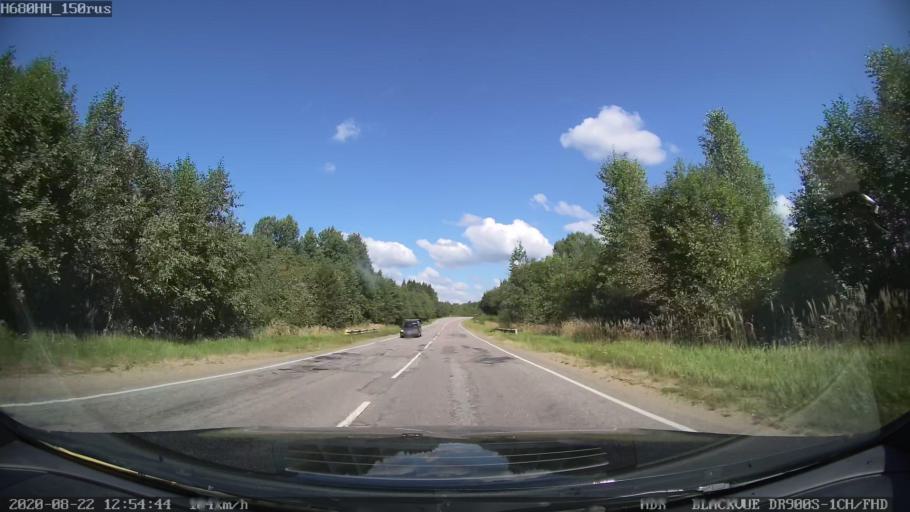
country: RU
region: Tverskaya
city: Rameshki
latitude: 57.5354
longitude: 36.2890
